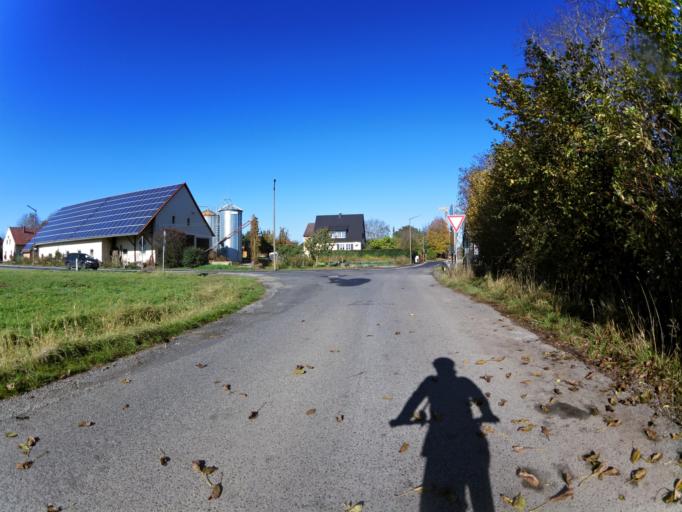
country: DE
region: Bavaria
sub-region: Regierungsbezirk Unterfranken
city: Geroldshausen
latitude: 49.6922
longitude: 9.9286
